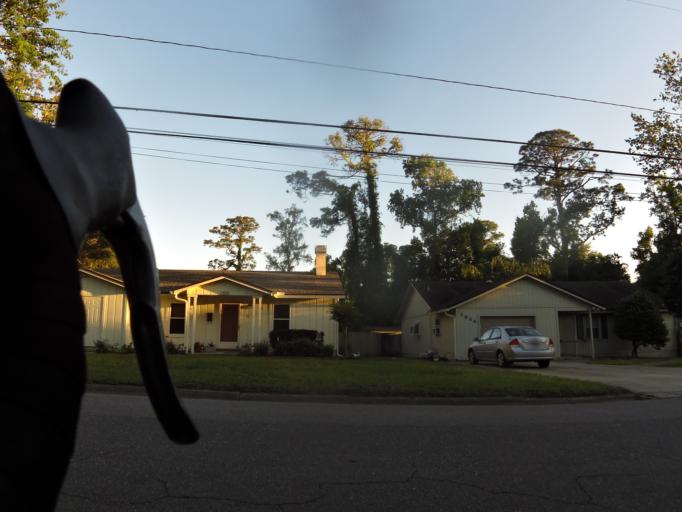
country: US
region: Florida
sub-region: Duval County
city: Jacksonville
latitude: 30.2588
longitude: -81.6397
